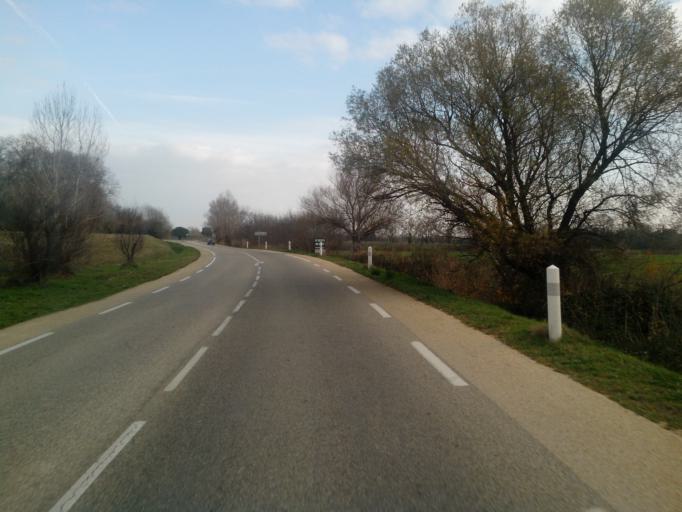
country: FR
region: Languedoc-Roussillon
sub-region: Departement du Gard
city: Saint-Gilles
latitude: 43.5822
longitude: 4.4449
